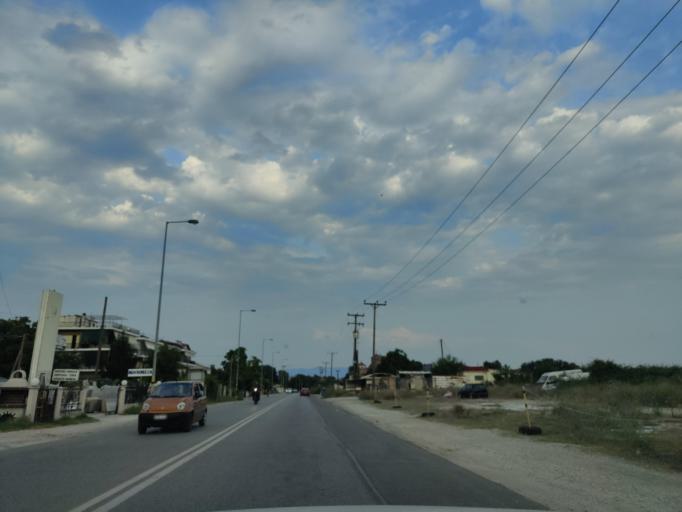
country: GR
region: East Macedonia and Thrace
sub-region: Nomos Dramas
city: Xiropotamos
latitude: 41.1556
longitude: 24.1094
